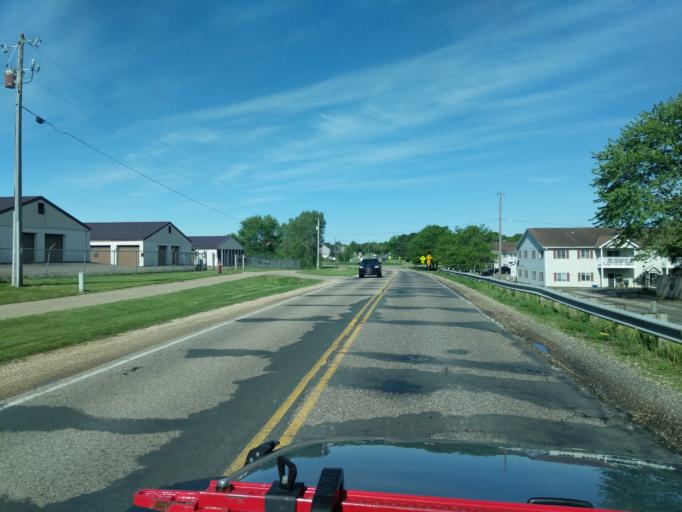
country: US
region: Wisconsin
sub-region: Pierce County
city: River Falls
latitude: 44.8411
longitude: -92.6057
